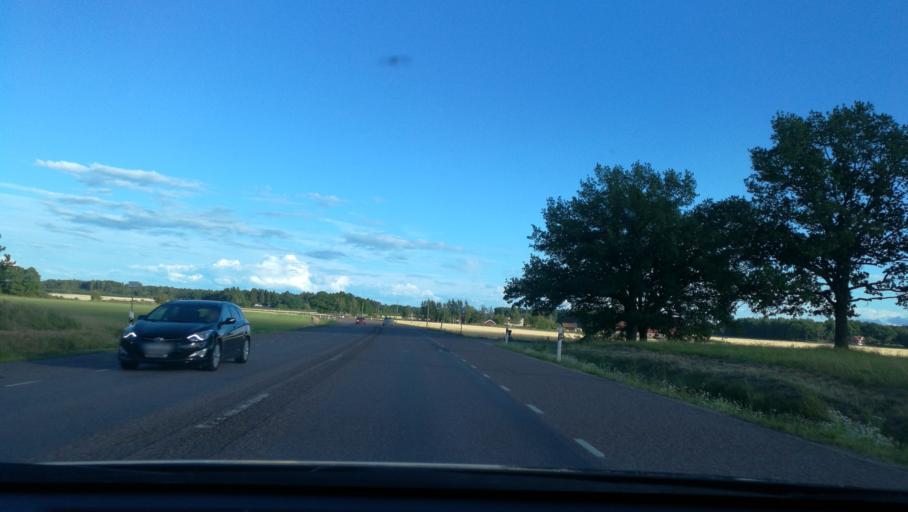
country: SE
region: Vaestmanland
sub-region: Kopings Kommun
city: Koping
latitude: 59.4659
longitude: 15.9941
